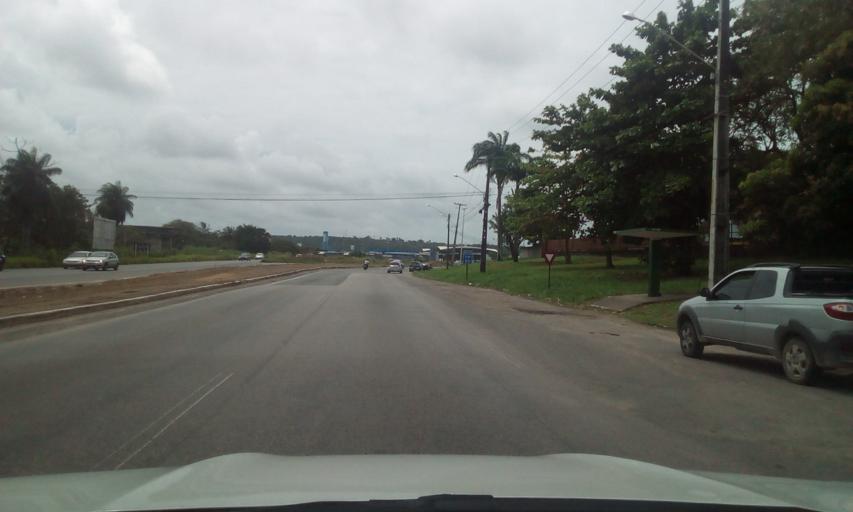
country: BR
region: Pernambuco
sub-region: Abreu E Lima
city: Abreu e Lima
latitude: -7.9248
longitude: -34.8967
